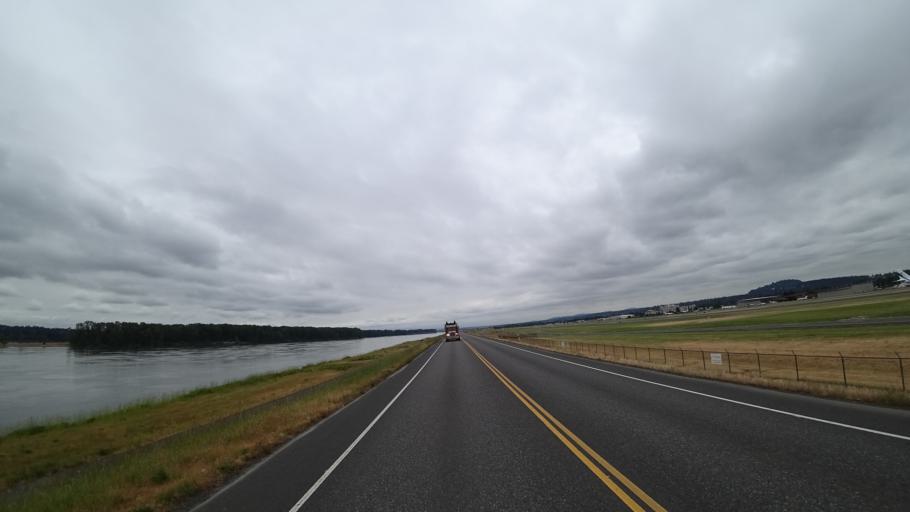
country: US
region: Washington
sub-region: Clark County
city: Orchards
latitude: 45.5915
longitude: -122.5809
